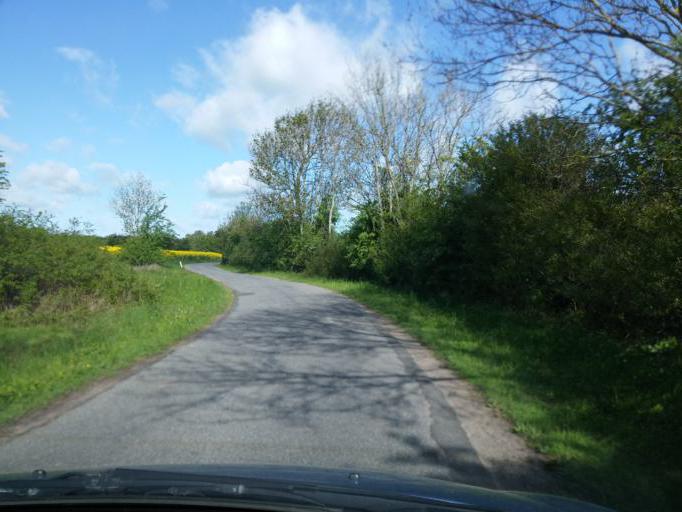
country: DK
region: South Denmark
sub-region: Kerteminde Kommune
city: Munkebo
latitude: 55.4121
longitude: 10.5420
